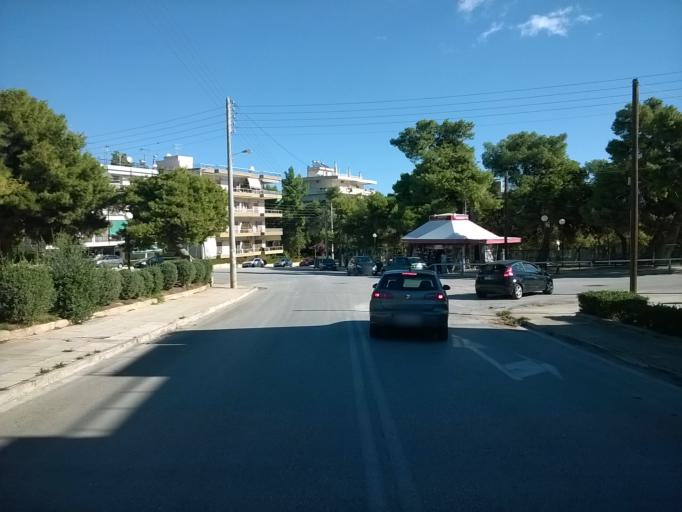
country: GR
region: Attica
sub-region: Nomarchia Anatolikis Attikis
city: Vouliagmeni
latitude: 37.8172
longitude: 23.7962
